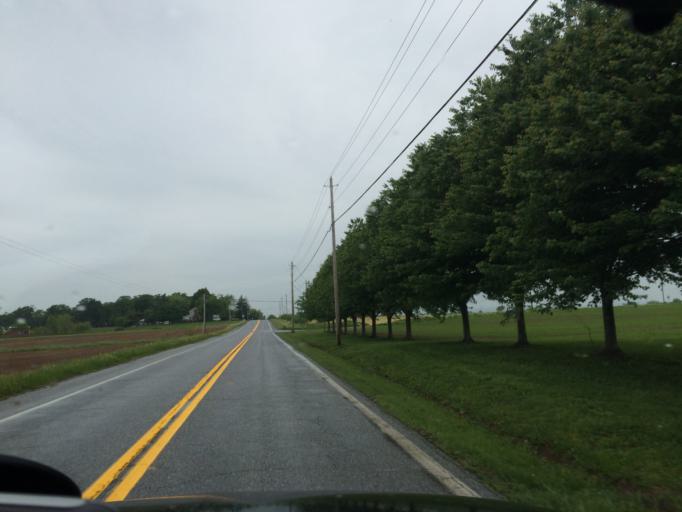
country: US
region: Maryland
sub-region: Carroll County
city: Taneytown
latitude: 39.5952
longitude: -77.1789
